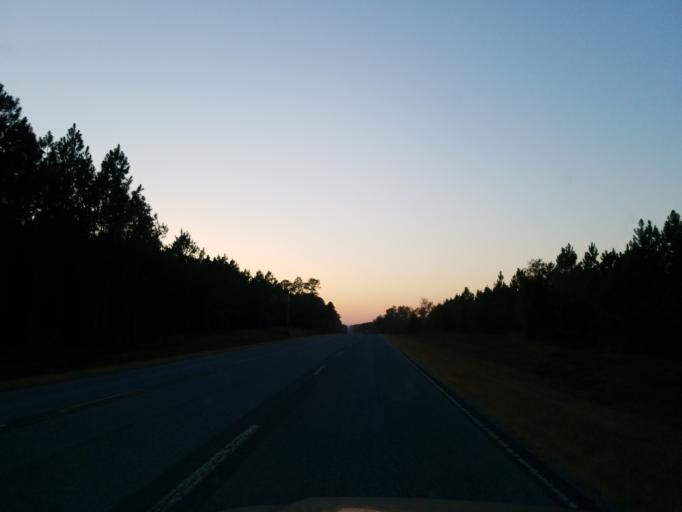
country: US
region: Georgia
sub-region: Ben Hill County
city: Fitzgerald
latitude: 31.7207
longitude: -83.4268
